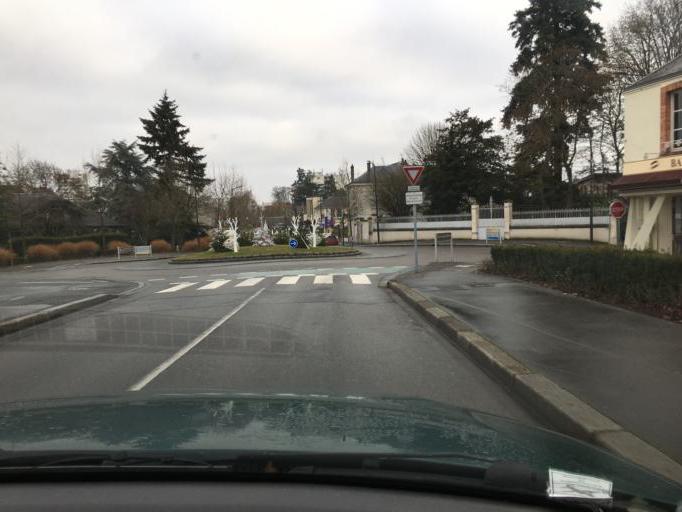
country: FR
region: Centre
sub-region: Departement du Loiret
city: Olivet
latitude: 47.8702
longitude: 1.9036
